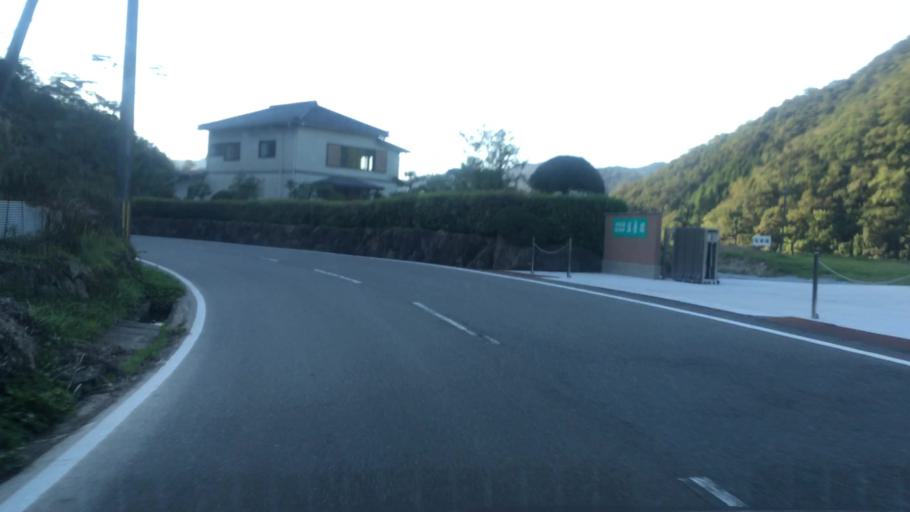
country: JP
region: Hyogo
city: Toyooka
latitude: 35.6159
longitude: 134.8261
